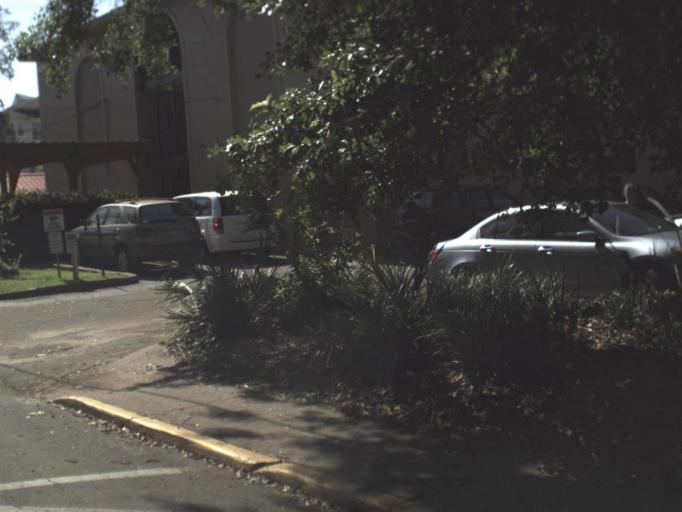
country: US
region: Florida
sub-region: Leon County
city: Tallahassee
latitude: 30.4375
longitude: -84.2920
